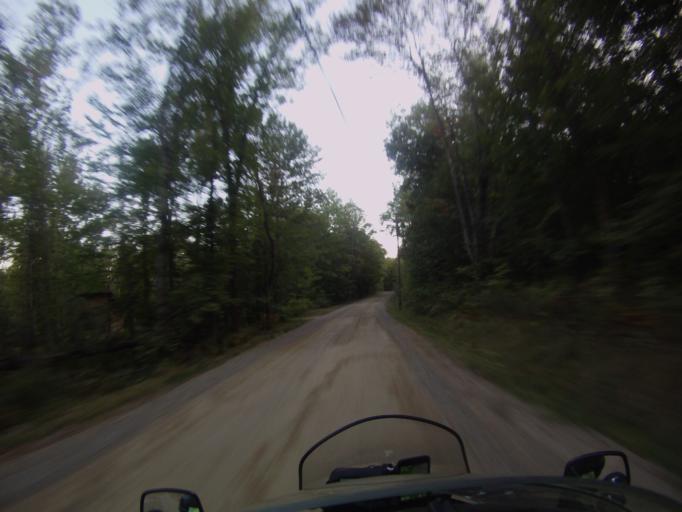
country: US
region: Vermont
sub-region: Addison County
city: Middlebury (village)
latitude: 43.9996
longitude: -73.0395
